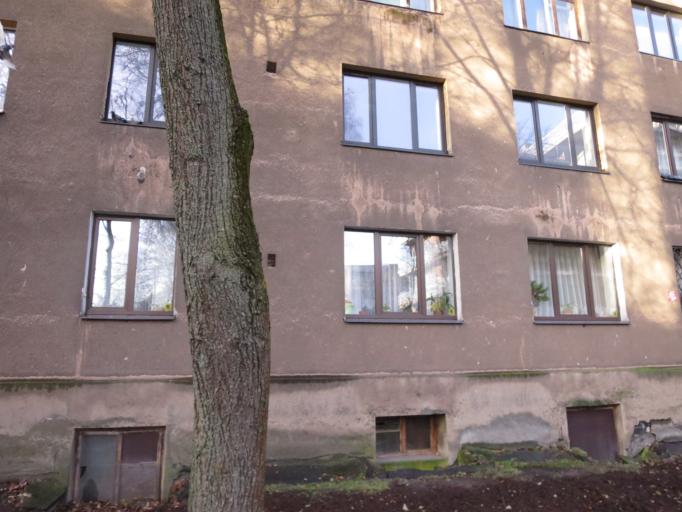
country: LV
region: Riga
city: Riga
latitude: 56.9658
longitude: 24.1272
